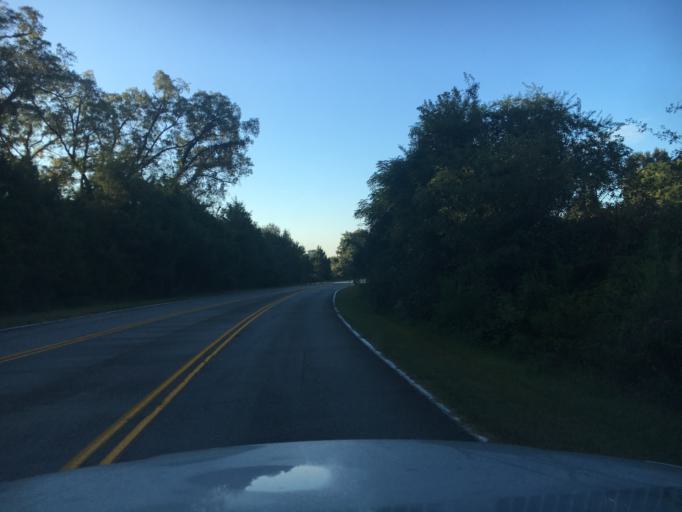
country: US
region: South Carolina
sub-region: Spartanburg County
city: Woodruff
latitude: 34.7993
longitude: -82.0151
